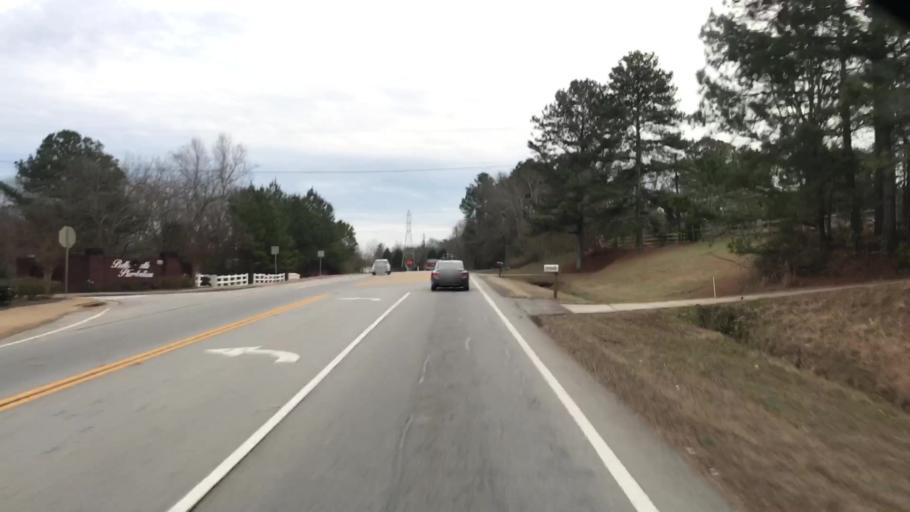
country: US
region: Georgia
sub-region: Barrow County
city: Winder
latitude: 34.0030
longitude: -83.7509
